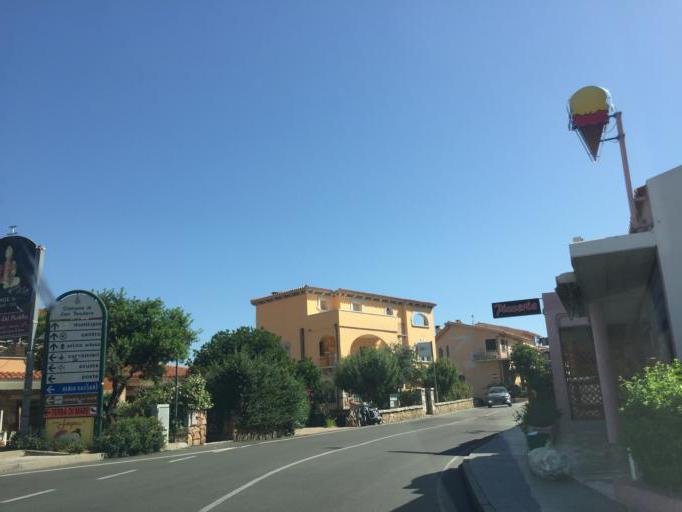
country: IT
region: Sardinia
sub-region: Provincia di Olbia-Tempio
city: San Teodoro
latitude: 40.7698
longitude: 9.6692
